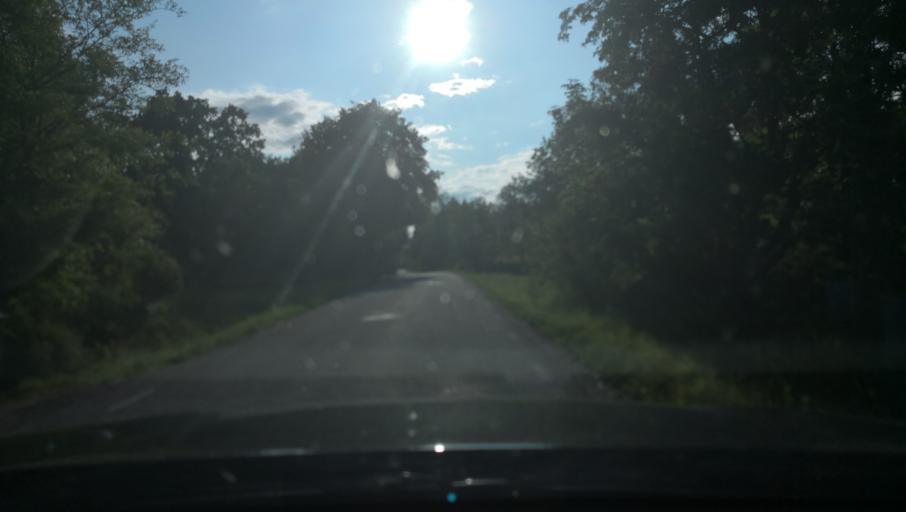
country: SE
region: Uppsala
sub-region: Osthammars Kommun
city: Osterbybruk
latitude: 60.0202
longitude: 17.9601
